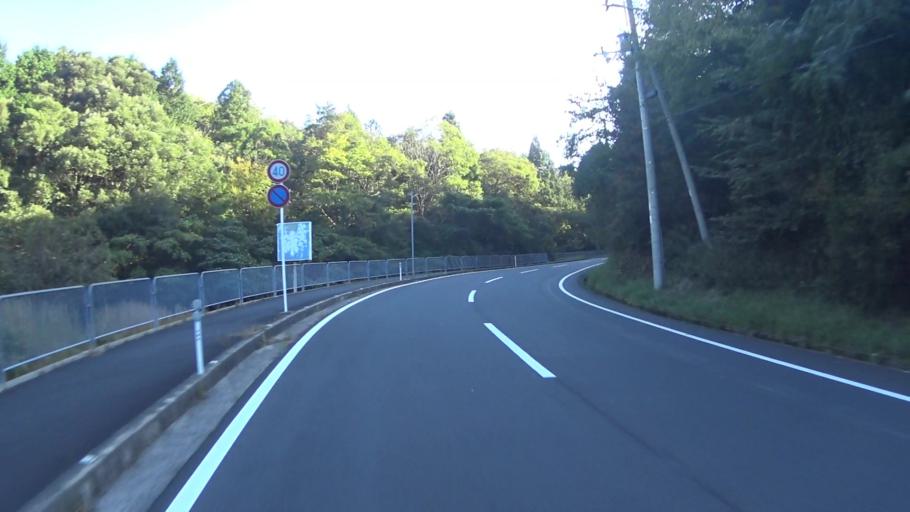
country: JP
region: Hyogo
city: Toyooka
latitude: 35.6193
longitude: 134.8841
